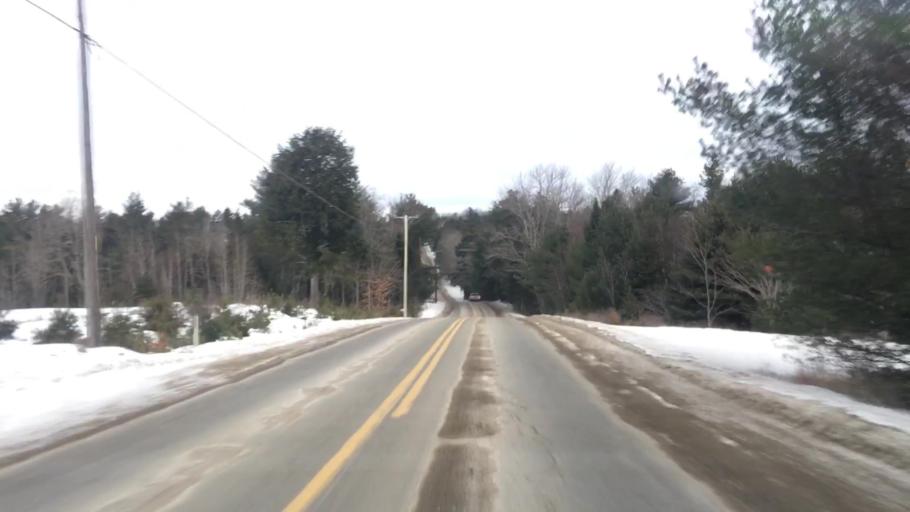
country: US
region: Maine
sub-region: Hancock County
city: Franklin
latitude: 44.8395
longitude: -68.3234
